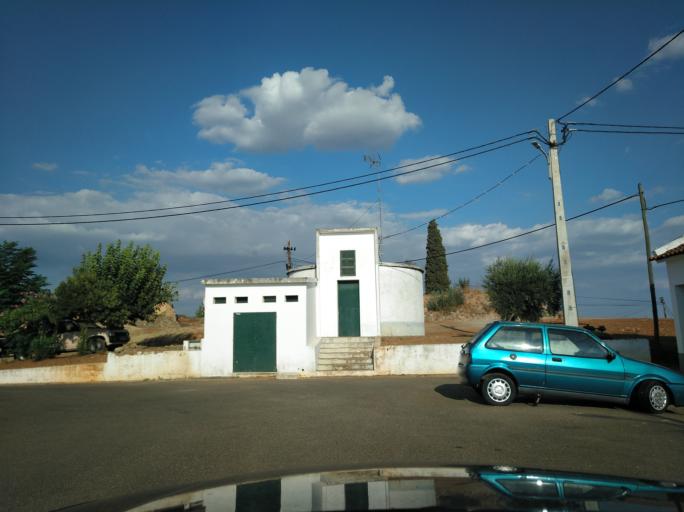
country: PT
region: Portalegre
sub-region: Campo Maior
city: Campo Maior
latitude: 39.0789
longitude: -7.0328
